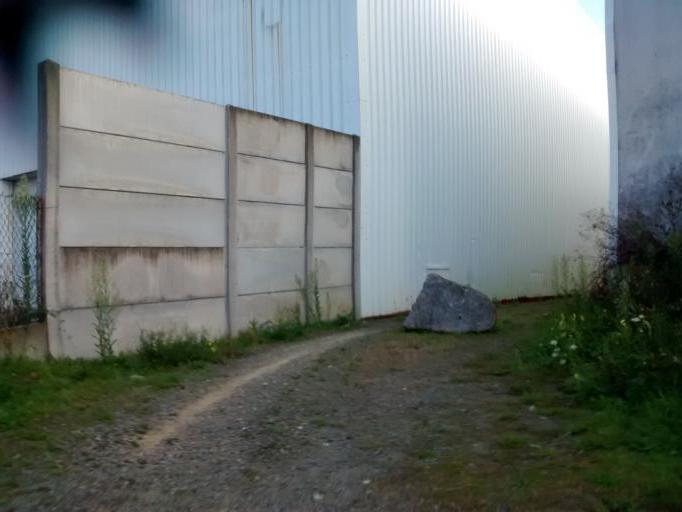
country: FR
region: Brittany
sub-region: Departement d'Ille-et-Vilaine
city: Chantepie
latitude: 48.1013
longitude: -1.6216
